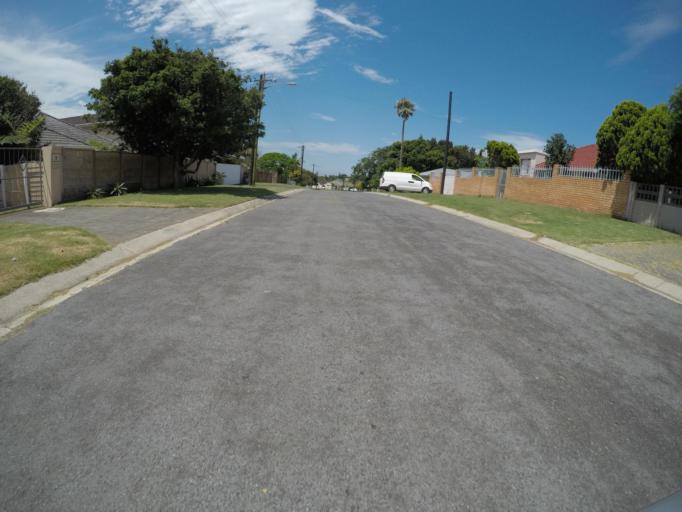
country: ZA
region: Eastern Cape
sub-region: Buffalo City Metropolitan Municipality
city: East London
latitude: -33.0322
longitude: 27.8644
